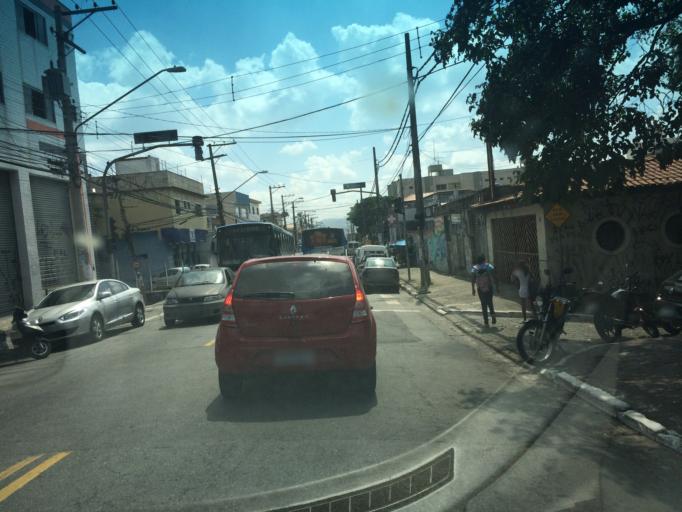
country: BR
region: Sao Paulo
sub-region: Guarulhos
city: Guarulhos
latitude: -23.4466
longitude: -46.5473
